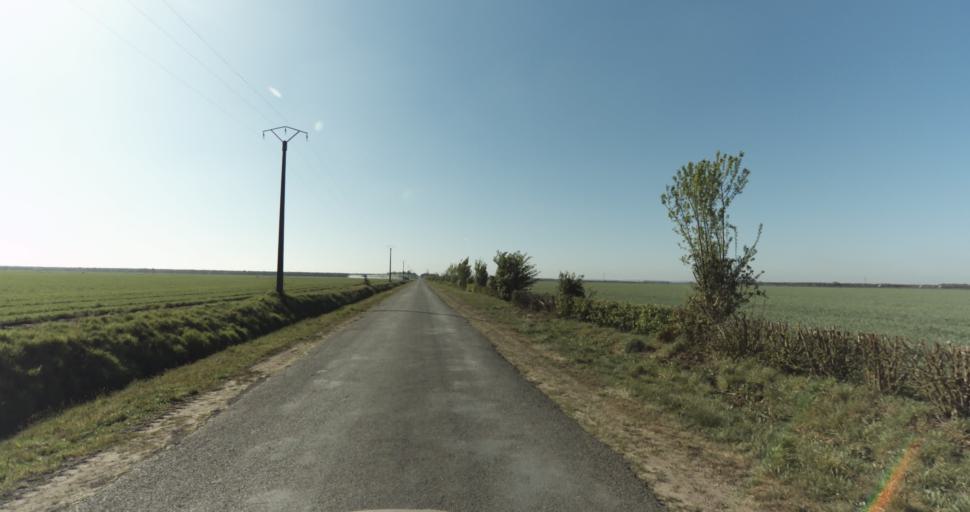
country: FR
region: Aquitaine
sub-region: Departement de la Gironde
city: Marcheprime
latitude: 44.7730
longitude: -0.8577
